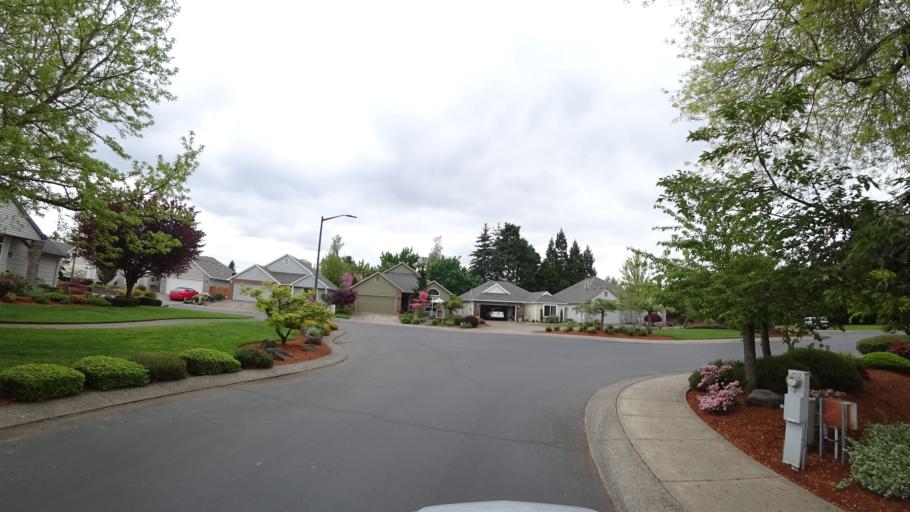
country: US
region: Oregon
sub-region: Washington County
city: Hillsboro
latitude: 45.5391
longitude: -122.9791
